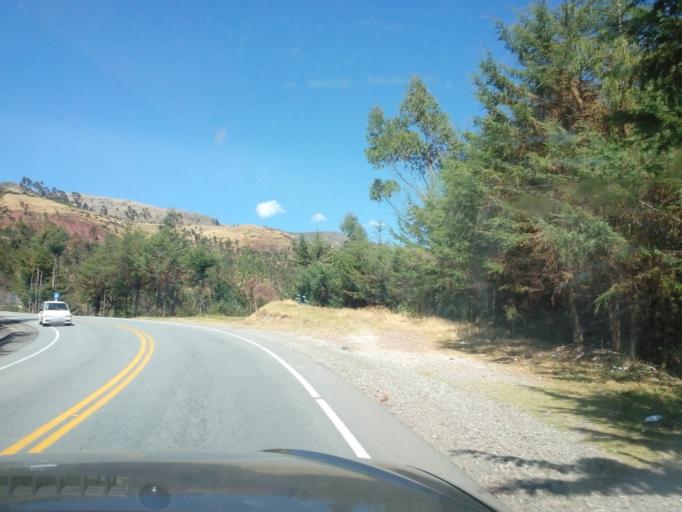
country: PE
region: Cusco
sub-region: Provincia de Anta
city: Limatambo
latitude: -13.4494
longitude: -72.3984
